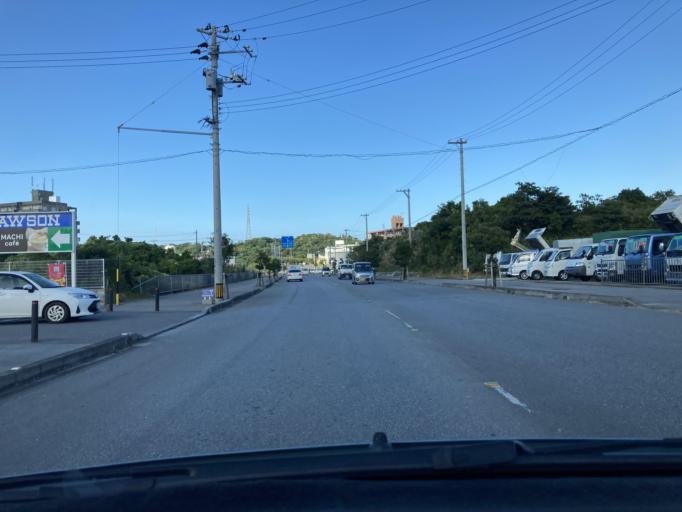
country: JP
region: Okinawa
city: Gushikawa
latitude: 26.3830
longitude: 127.8391
